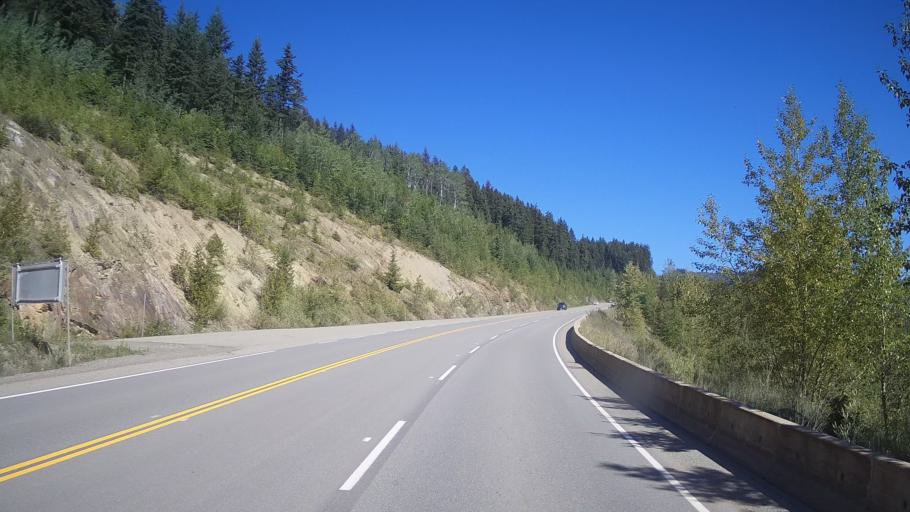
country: CA
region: British Columbia
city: Kamloops
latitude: 51.4706
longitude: -120.2551
